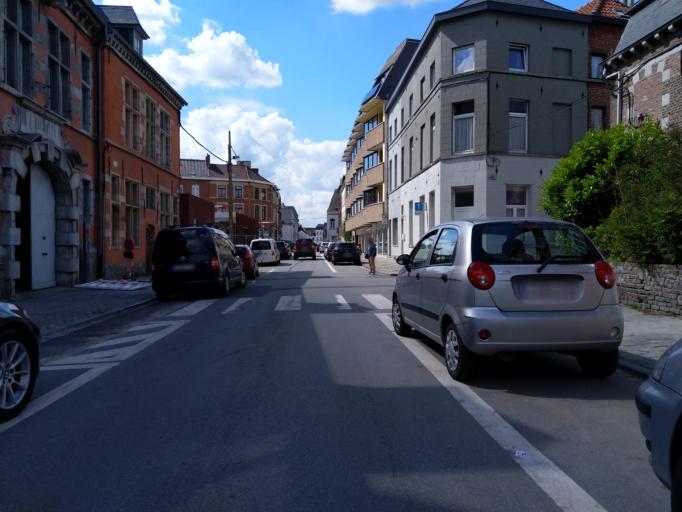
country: BE
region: Wallonia
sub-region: Province du Hainaut
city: Mons
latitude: 50.4501
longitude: 3.9473
